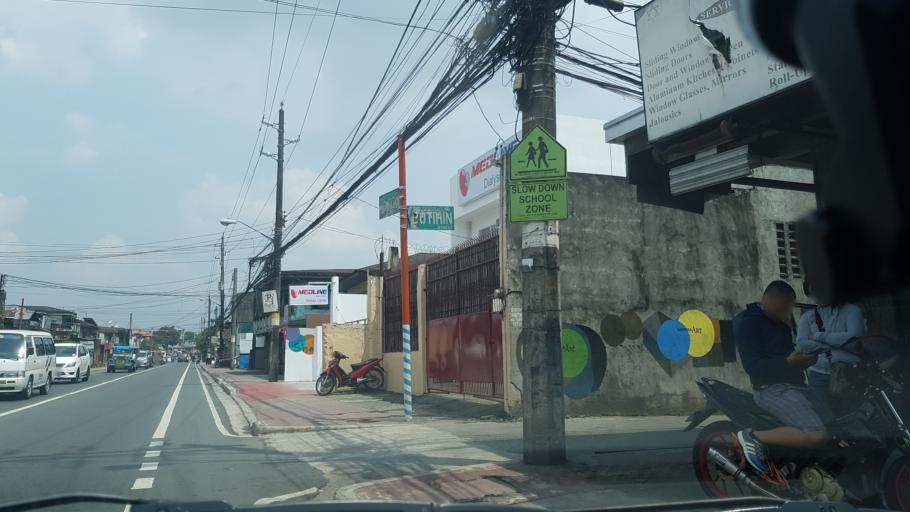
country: PH
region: Metro Manila
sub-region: Marikina
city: Calumpang
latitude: 14.6541
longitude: 121.1032
